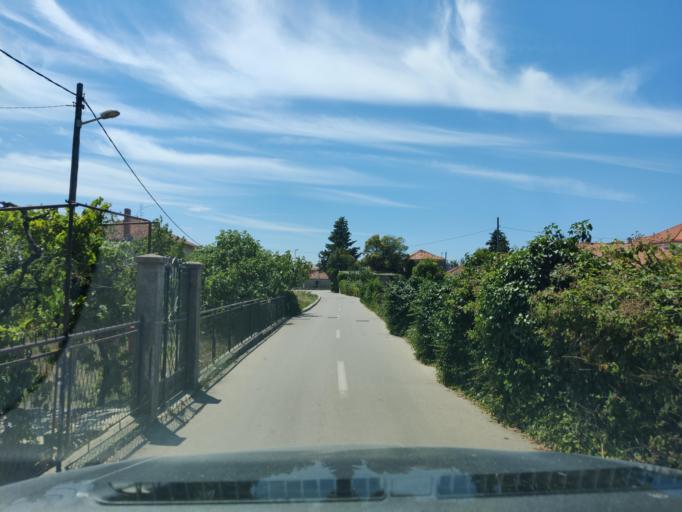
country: HR
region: Zadarska
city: Zadar
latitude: 44.1055
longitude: 15.2461
